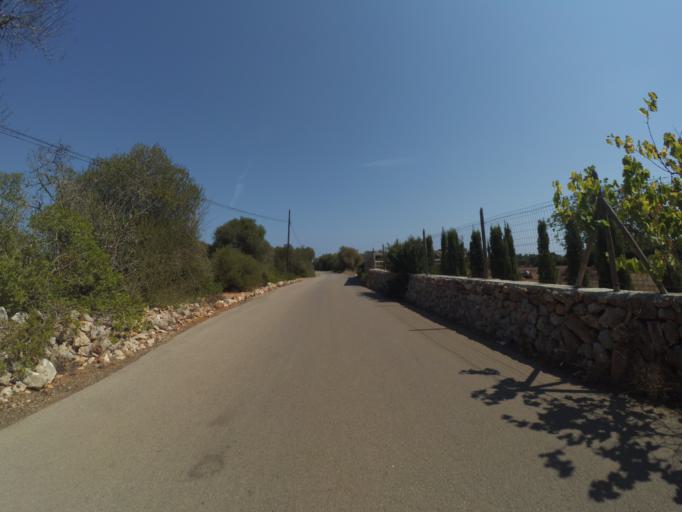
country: ES
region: Balearic Islands
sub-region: Illes Balears
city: Santanyi
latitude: 39.3930
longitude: 3.2407
